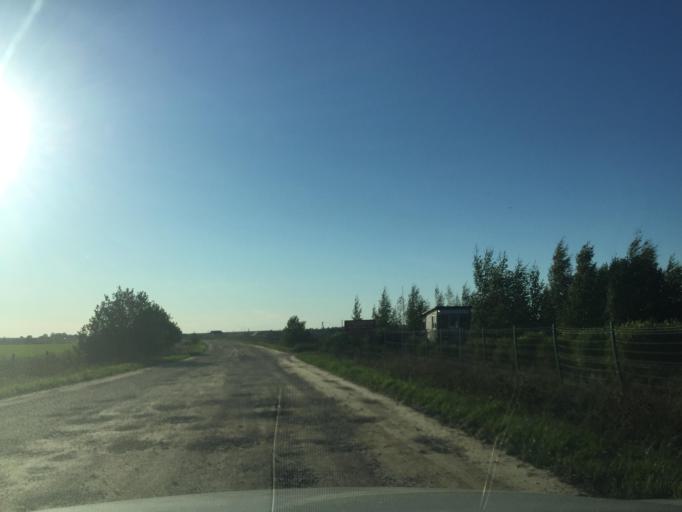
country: RU
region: Leningrad
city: Siverskiy
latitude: 59.3317
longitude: 30.0159
